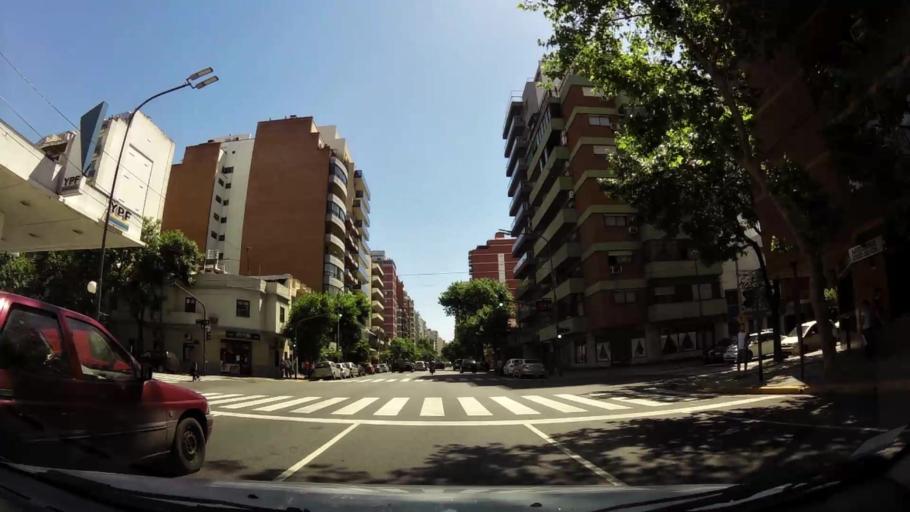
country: AR
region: Buenos Aires F.D.
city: Colegiales
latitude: -34.6223
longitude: -58.4291
